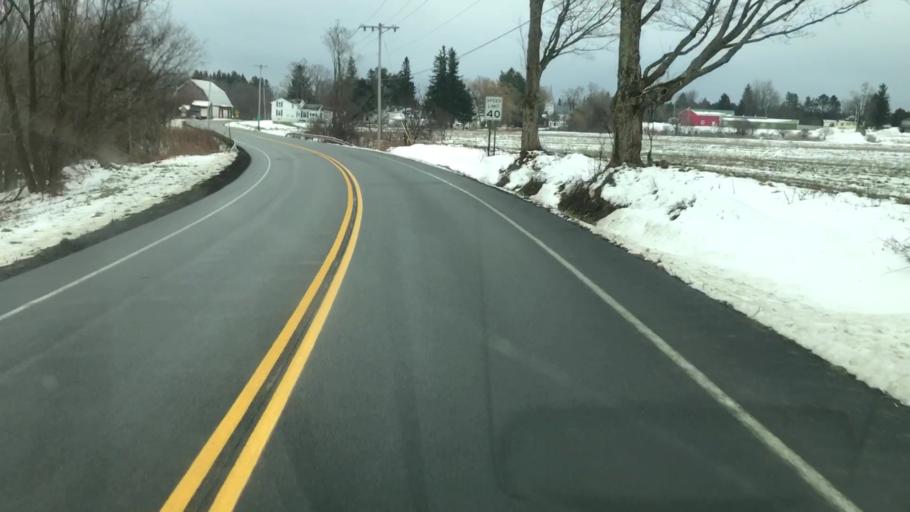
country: US
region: New York
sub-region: Cayuga County
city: Moravia
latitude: 42.8016
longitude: -76.3493
